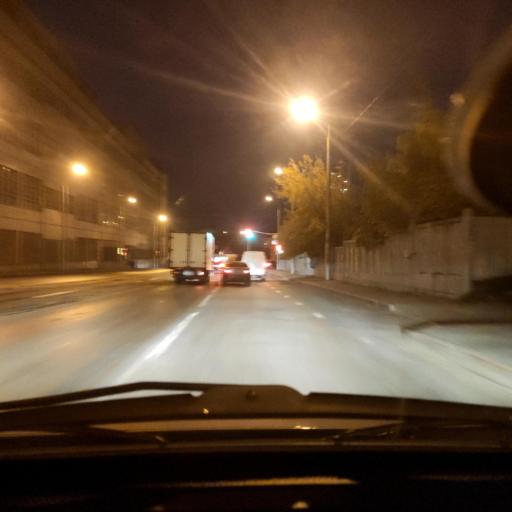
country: RU
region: Bashkortostan
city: Ufa
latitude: 54.7366
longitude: 55.9397
